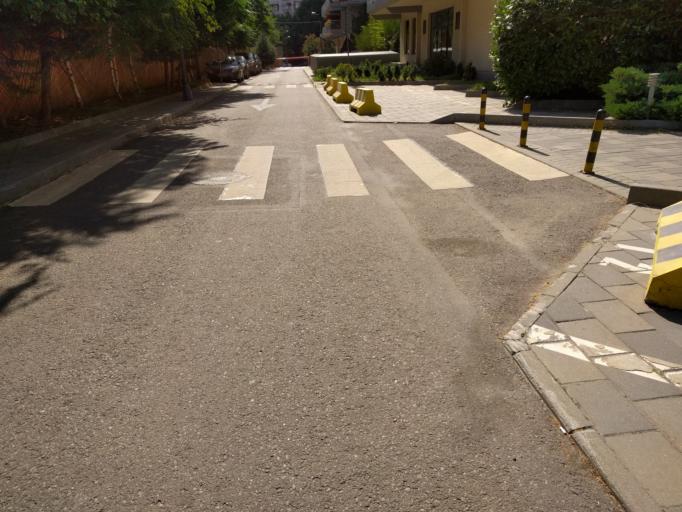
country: RO
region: Bucuresti
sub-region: Municipiul Bucuresti
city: Bucharest
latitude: 44.4231
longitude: 26.1399
